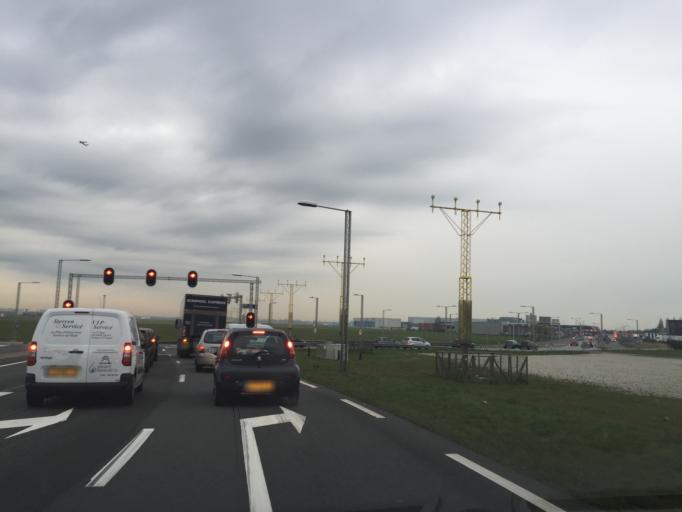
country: NL
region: North Holland
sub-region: Gemeente Aalsmeer
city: Aalsmeer
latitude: 52.2829
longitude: 4.7763
